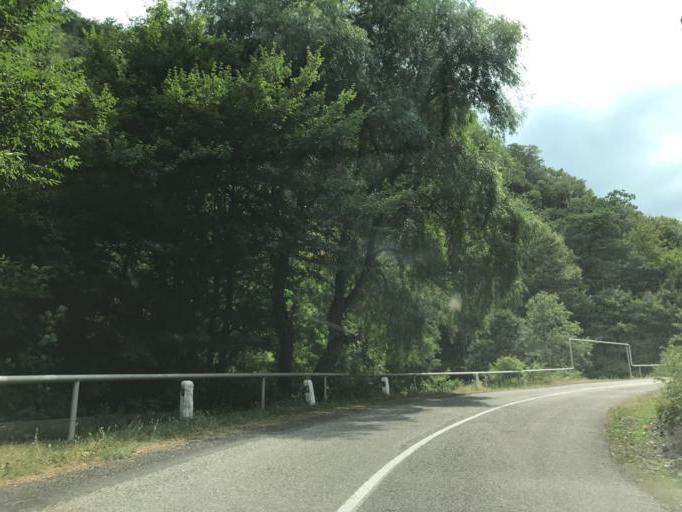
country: AM
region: Tavush
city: Haghartsin
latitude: 40.7396
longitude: 45.0217
